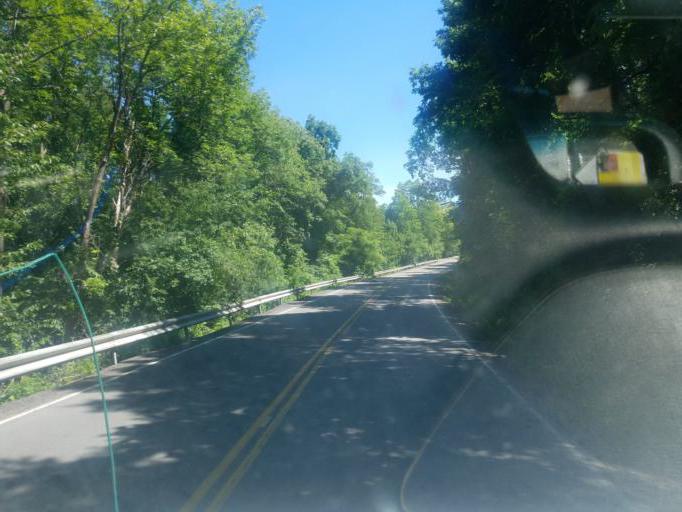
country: US
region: New York
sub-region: Ontario County
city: Canandaigua
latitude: 42.7366
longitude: -77.3239
